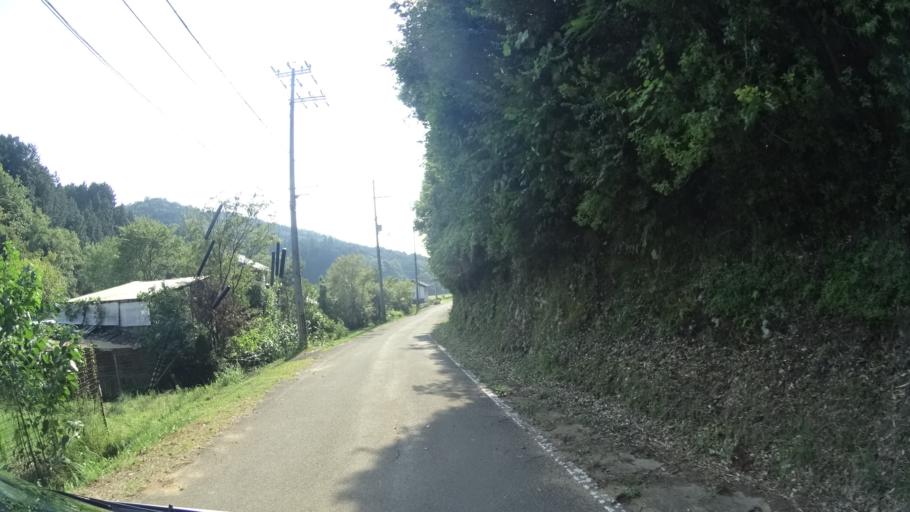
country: JP
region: Kyoto
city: Maizuru
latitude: 35.4339
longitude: 135.2779
